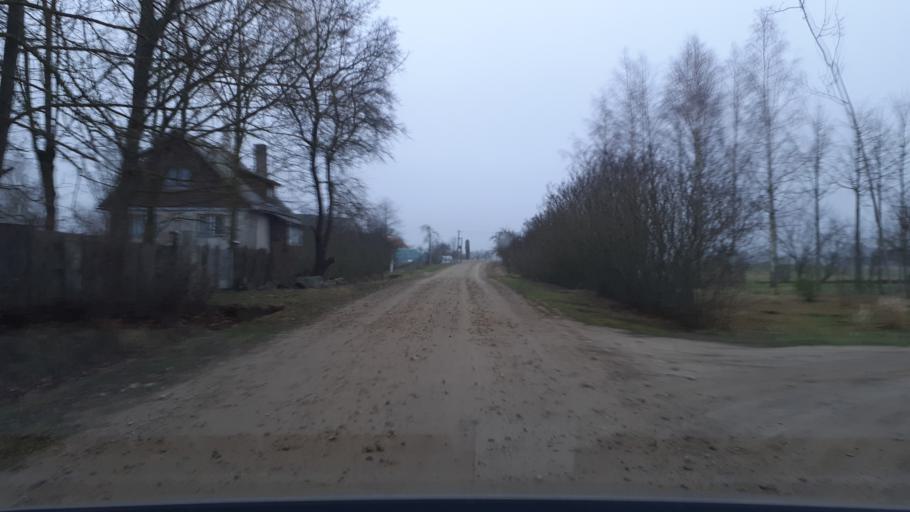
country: LV
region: Talsu Rajons
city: Sabile
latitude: 56.9560
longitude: 22.4027
